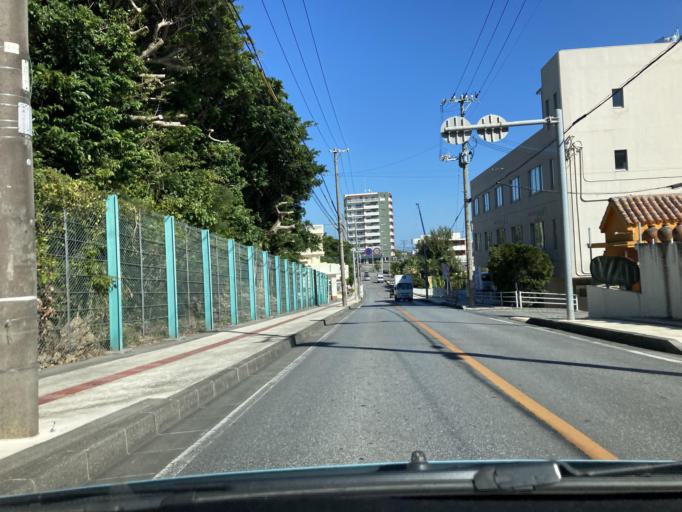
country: JP
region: Okinawa
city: Okinawa
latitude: 26.3304
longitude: 127.8047
